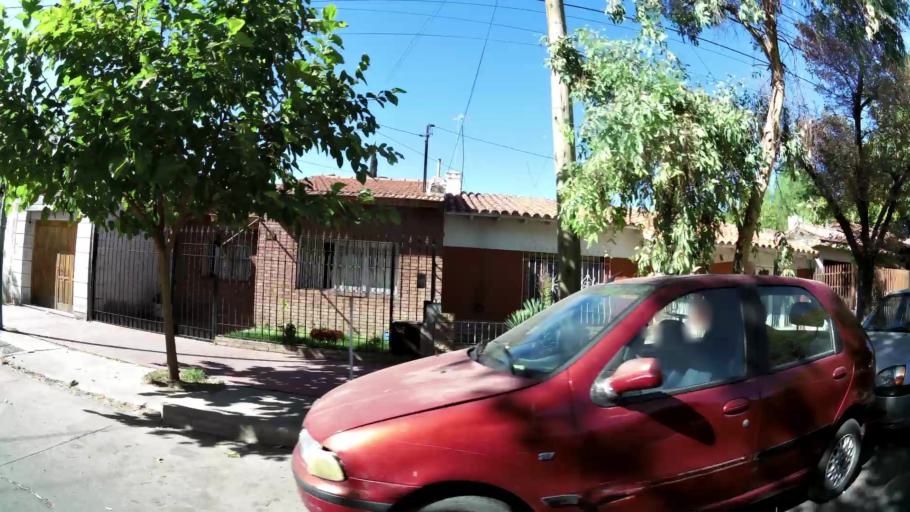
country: AR
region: Mendoza
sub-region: Departamento de Godoy Cruz
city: Godoy Cruz
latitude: -32.9251
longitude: -68.8517
